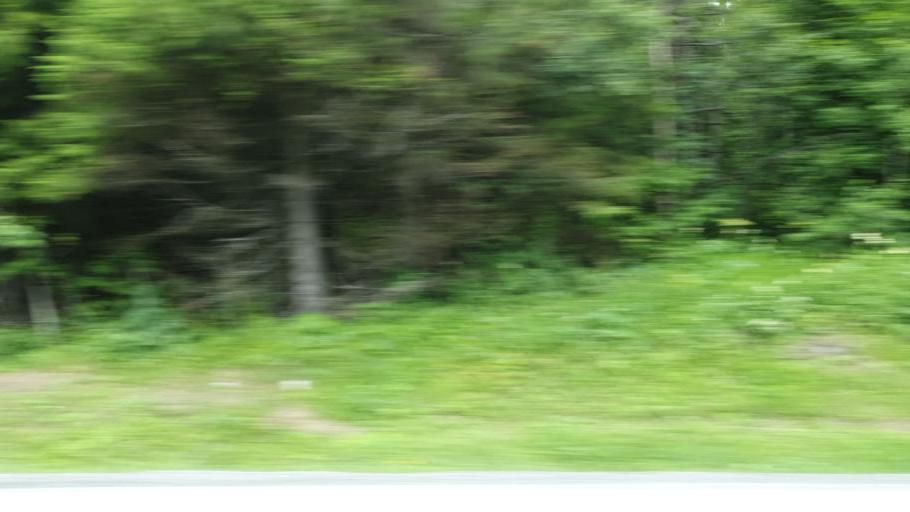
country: NO
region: Sor-Trondelag
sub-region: Rennebu
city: Berkak
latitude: 62.8692
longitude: 10.0817
